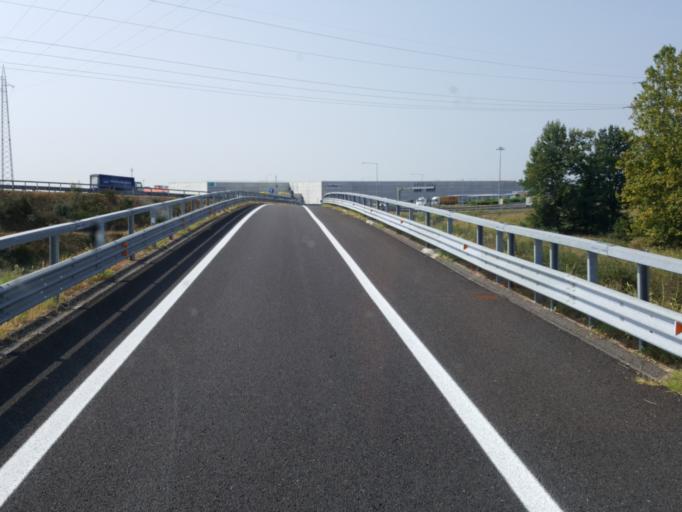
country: IT
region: Lombardy
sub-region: Citta metropolitana di Milano
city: Pozzuolo Martesana
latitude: 45.5187
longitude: 9.4396
